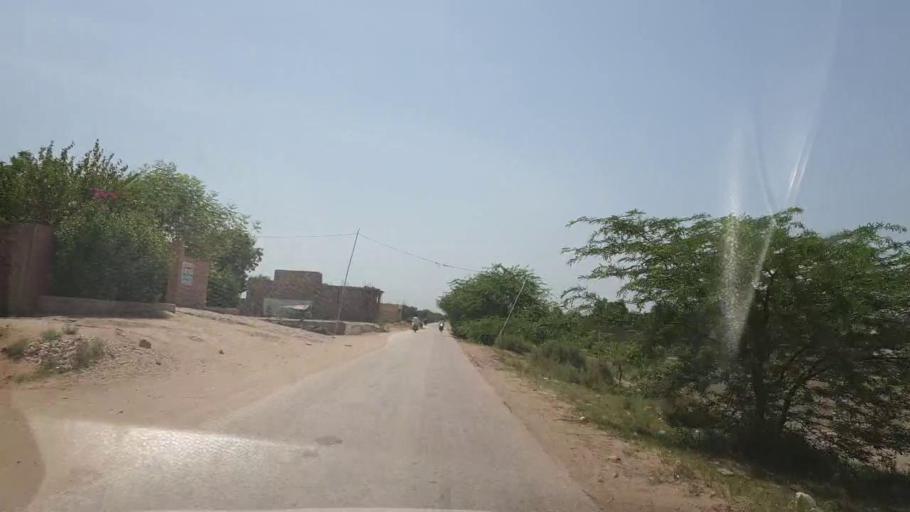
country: PK
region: Sindh
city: Bozdar
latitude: 27.0724
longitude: 68.6065
